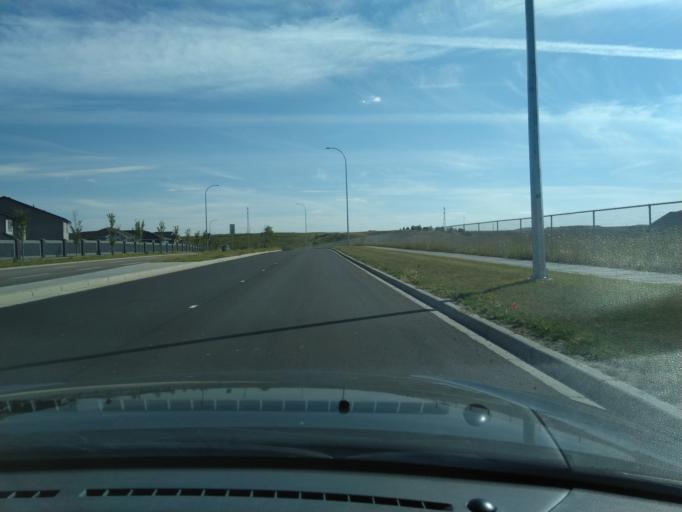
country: CA
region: Alberta
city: Calgary
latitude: 51.1753
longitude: -114.1762
